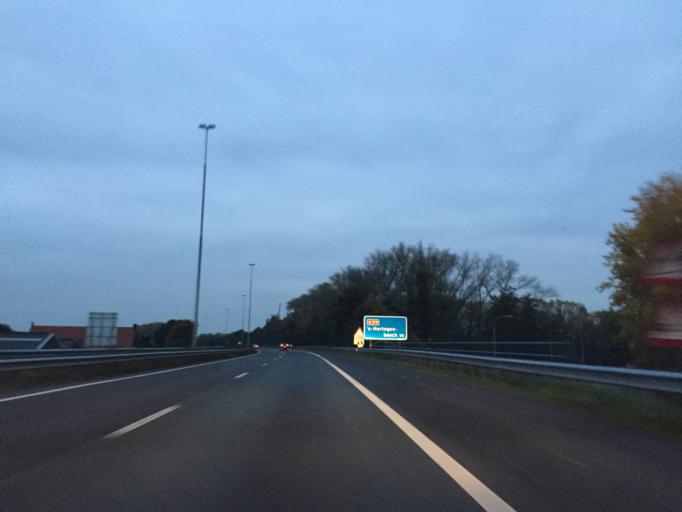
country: NL
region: North Brabant
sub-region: Gemeente Waalwijk
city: Waalwijk
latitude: 51.6928
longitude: 5.1104
